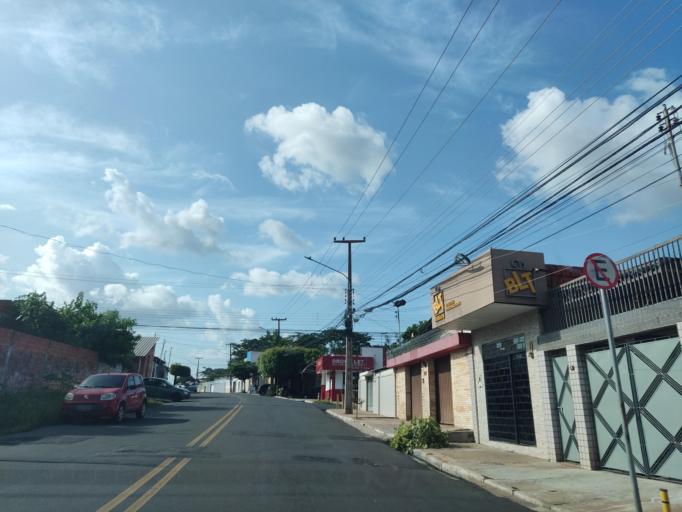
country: BR
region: Piaui
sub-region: Teresina
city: Teresina
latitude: -5.0799
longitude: -42.8029
